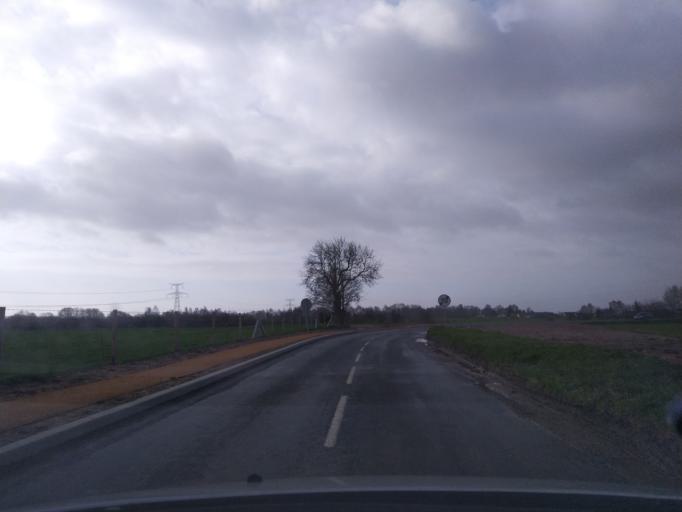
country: FR
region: Haute-Normandie
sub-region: Departement de la Seine-Maritime
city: Roumare
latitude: 49.5155
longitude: 0.9870
